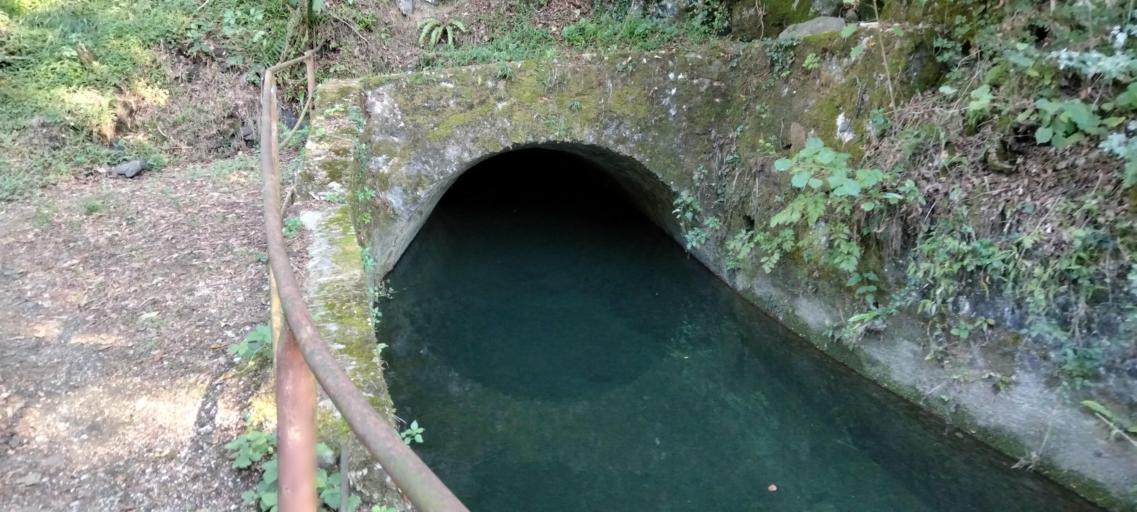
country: IT
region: Veneto
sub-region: Provincia di Vicenza
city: Calvene
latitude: 45.7632
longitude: 11.4915
